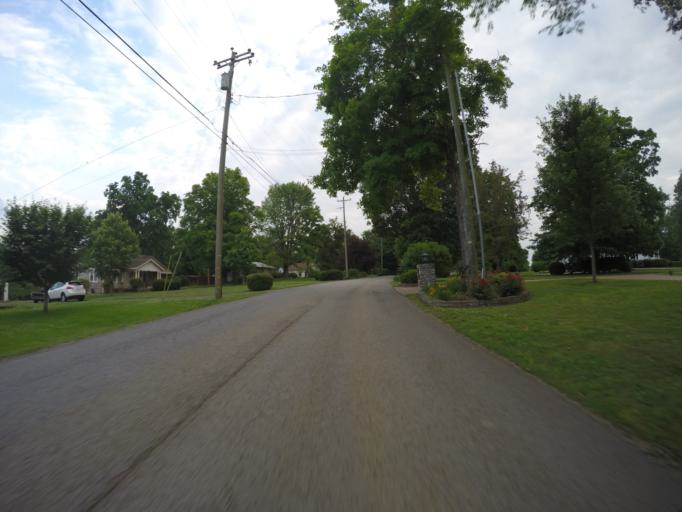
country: US
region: Tennessee
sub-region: Davidson County
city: Lakewood
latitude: 36.2407
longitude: -86.6256
